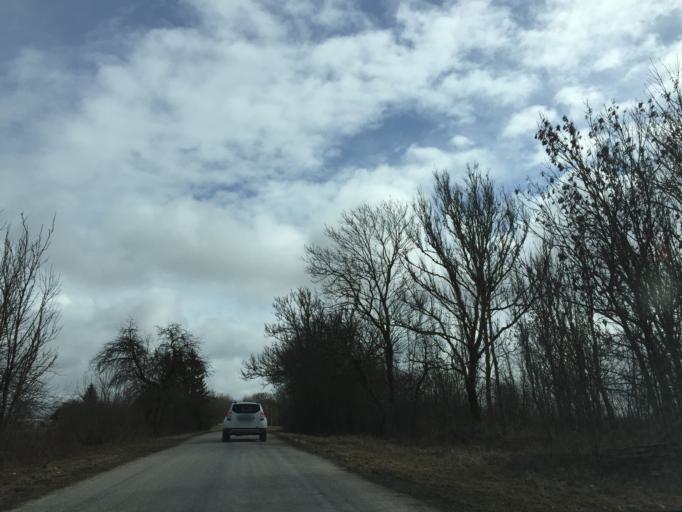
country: EE
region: Laeaene
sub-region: Lihula vald
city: Lihula
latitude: 58.7369
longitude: 23.8350
